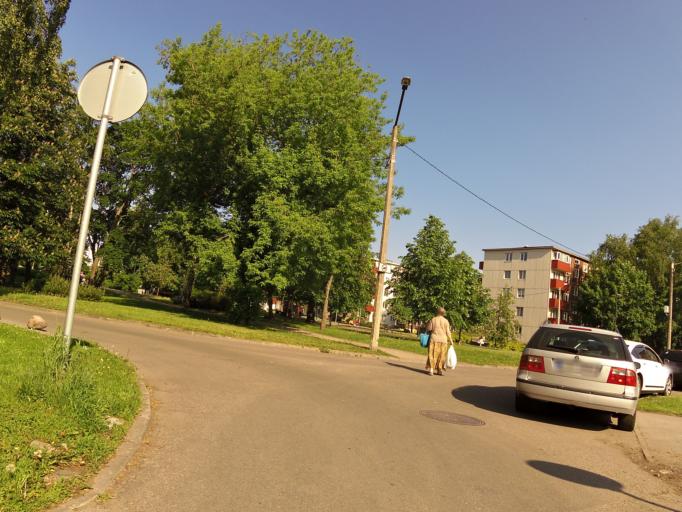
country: EE
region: Harju
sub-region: Tallinna linn
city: Tallinn
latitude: 59.4525
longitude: 24.7107
